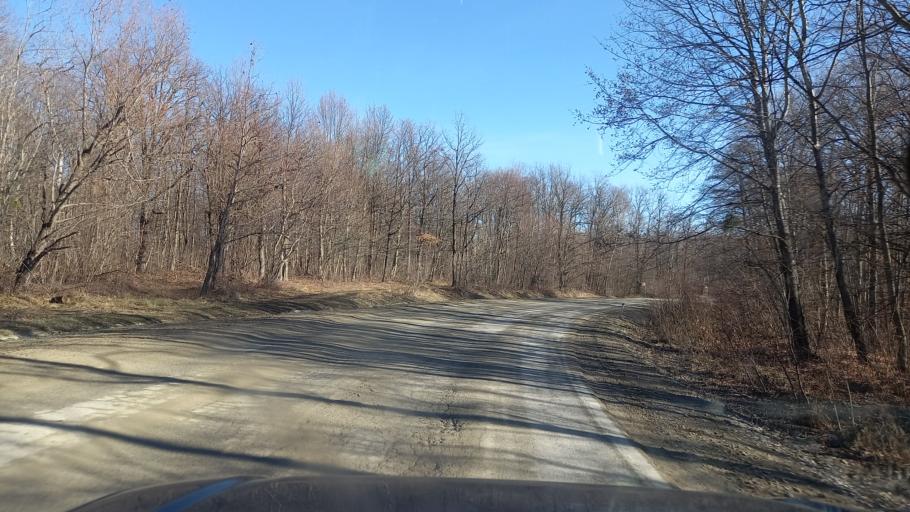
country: RU
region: Adygeya
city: Kamennomostskiy
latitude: 44.2837
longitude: 40.2633
